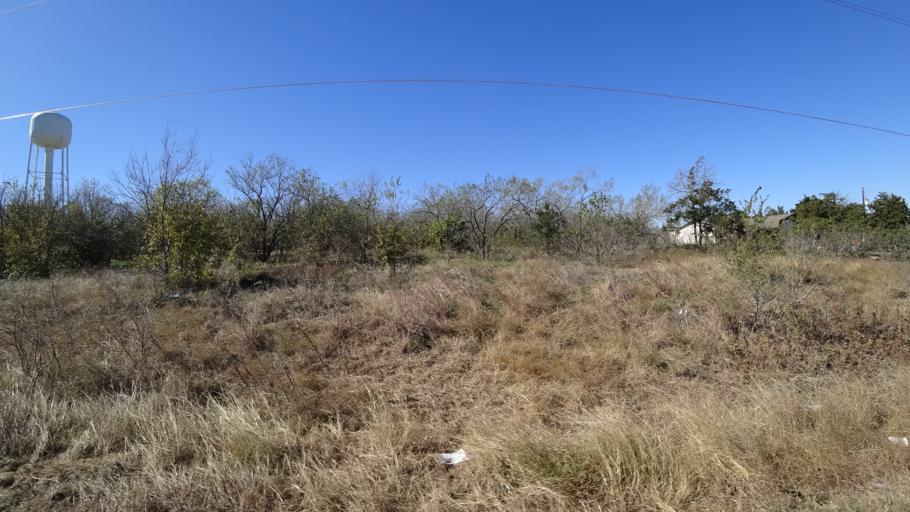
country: US
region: Texas
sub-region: Travis County
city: Garfield
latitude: 30.1005
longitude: -97.5986
